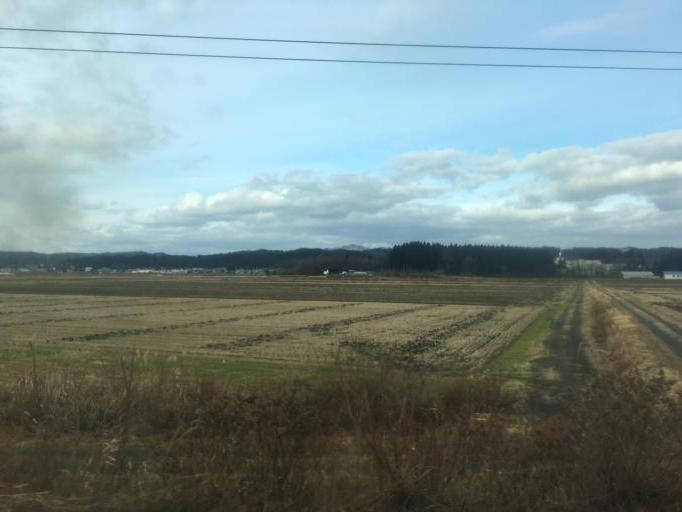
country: JP
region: Akita
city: Takanosu
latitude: 40.2478
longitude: 140.3941
